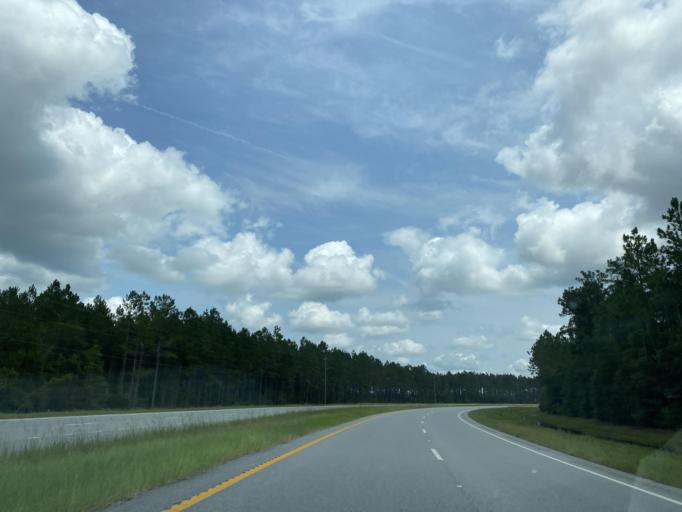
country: US
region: Georgia
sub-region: Ware County
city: Deenwood
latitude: 31.2709
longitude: -82.4363
